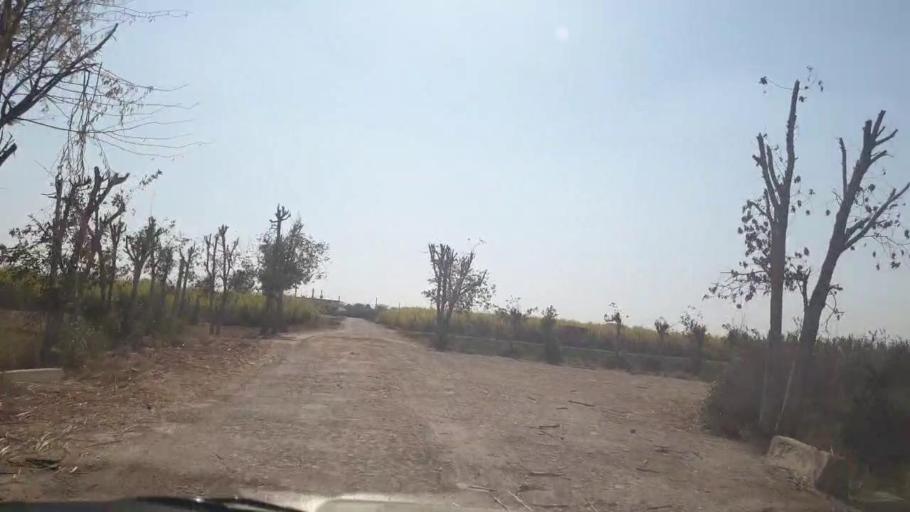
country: PK
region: Sindh
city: Mirpur Khas
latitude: 25.4742
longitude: 69.1265
